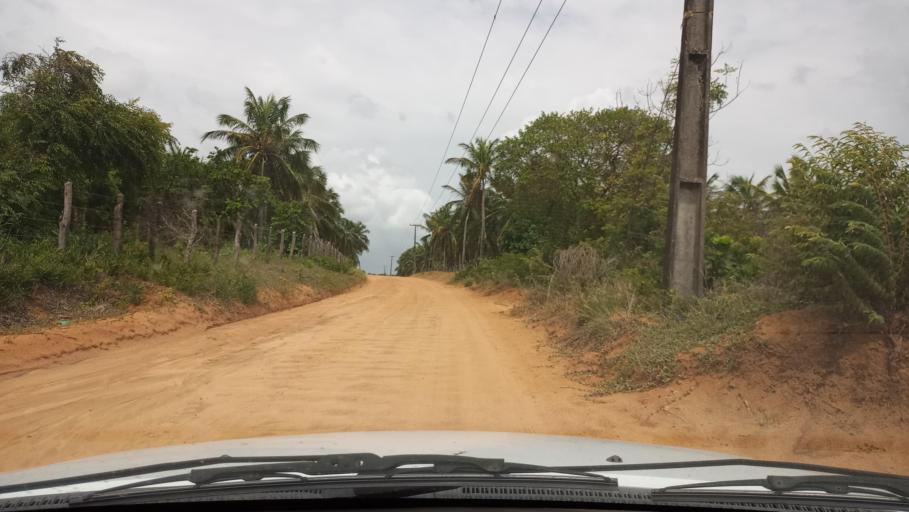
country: BR
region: Rio Grande do Norte
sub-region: Maxaranguape
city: Sao Miguel
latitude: -5.4837
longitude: -35.3137
